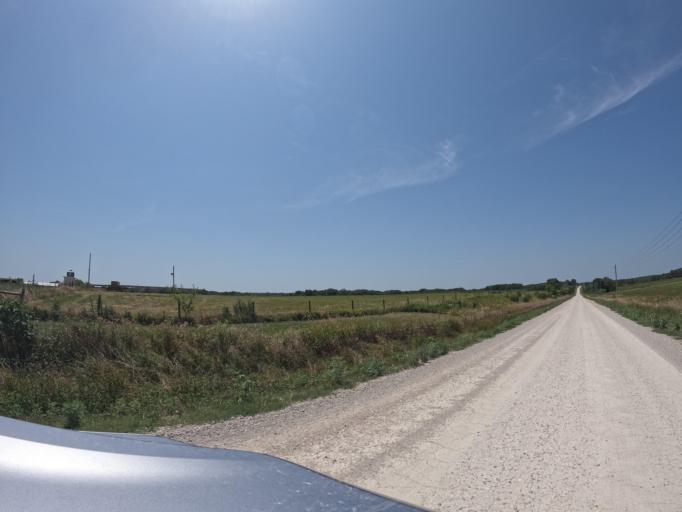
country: US
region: Iowa
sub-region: Henry County
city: Mount Pleasant
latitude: 40.9085
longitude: -91.6511
